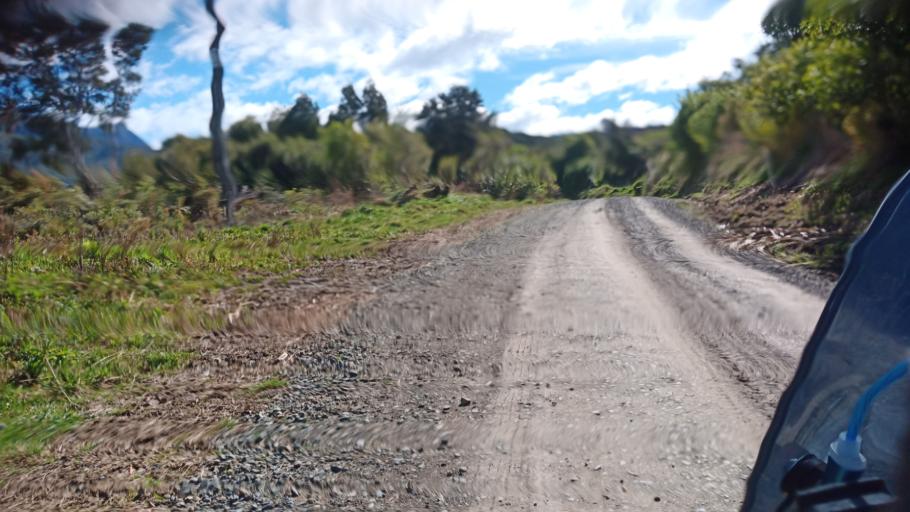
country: NZ
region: Hawke's Bay
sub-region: Wairoa District
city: Wairoa
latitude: -38.8206
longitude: 177.1618
